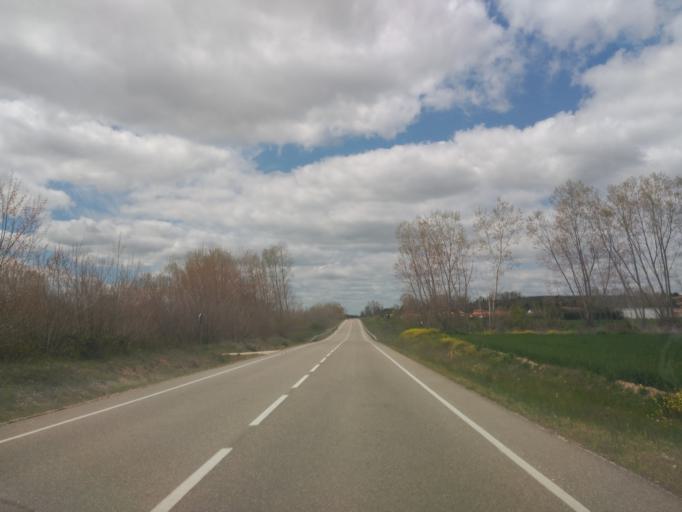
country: ES
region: Castille and Leon
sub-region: Provincia de Salamanca
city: Valverdon
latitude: 41.0483
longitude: -5.7749
